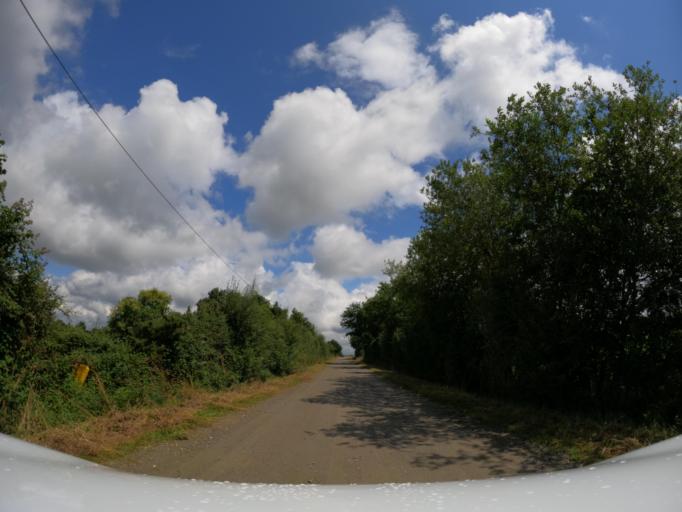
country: FR
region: Pays de la Loire
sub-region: Departement de la Loire-Atlantique
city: Saint-Mars-du-Desert
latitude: 47.3919
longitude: -1.4033
